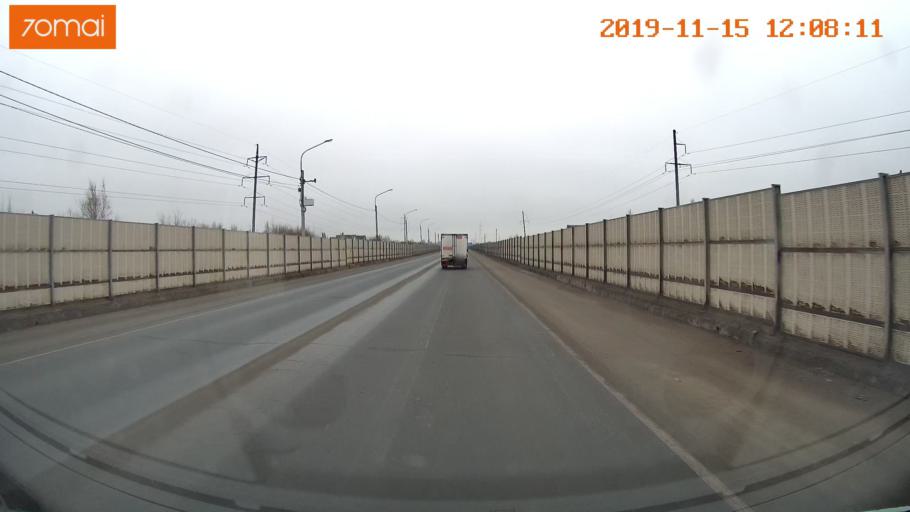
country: RU
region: Vologda
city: Vologda
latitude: 59.2289
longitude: 39.7747
